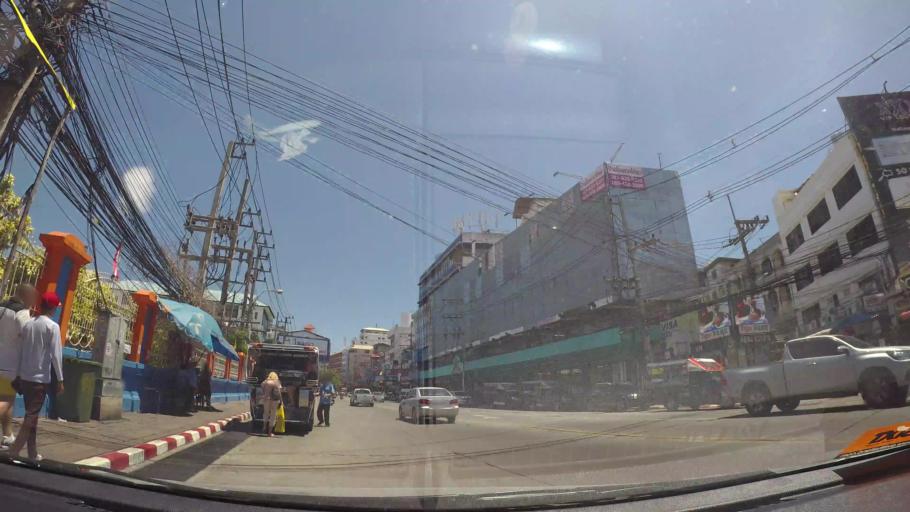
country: TH
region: Chon Buri
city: Phatthaya
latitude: 12.9261
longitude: 100.8754
